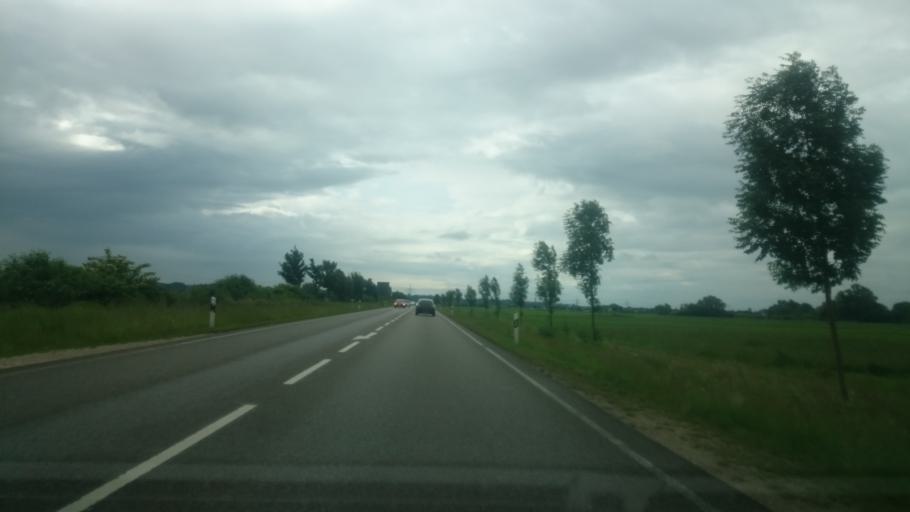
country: DE
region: Bavaria
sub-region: Swabia
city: Friedberg
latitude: 48.3925
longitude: 10.9492
